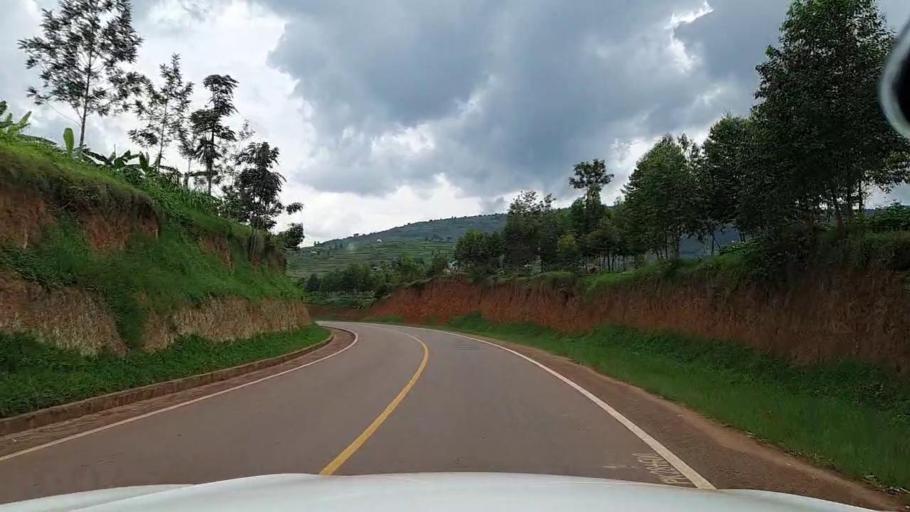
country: RW
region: Kigali
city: Kigali
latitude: -1.7819
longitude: 30.1305
